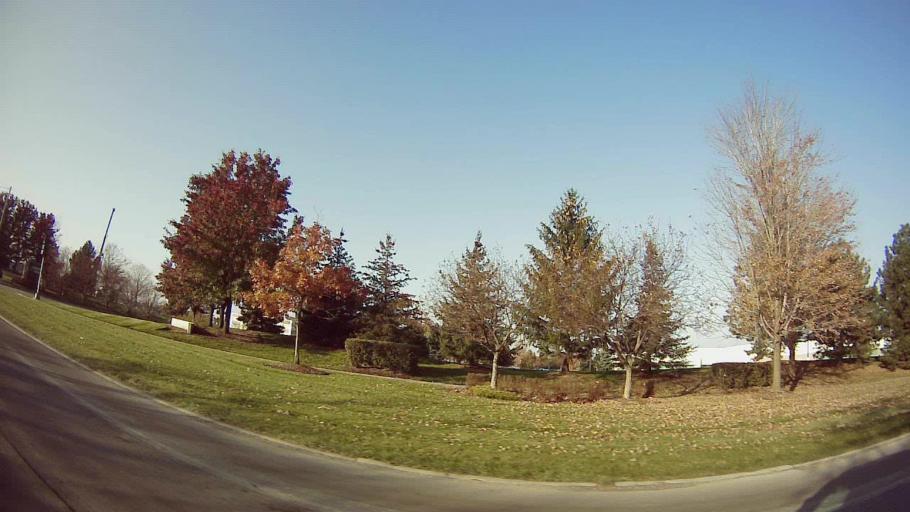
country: US
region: Michigan
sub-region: Wayne County
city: Dearborn
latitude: 42.3304
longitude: -83.1959
